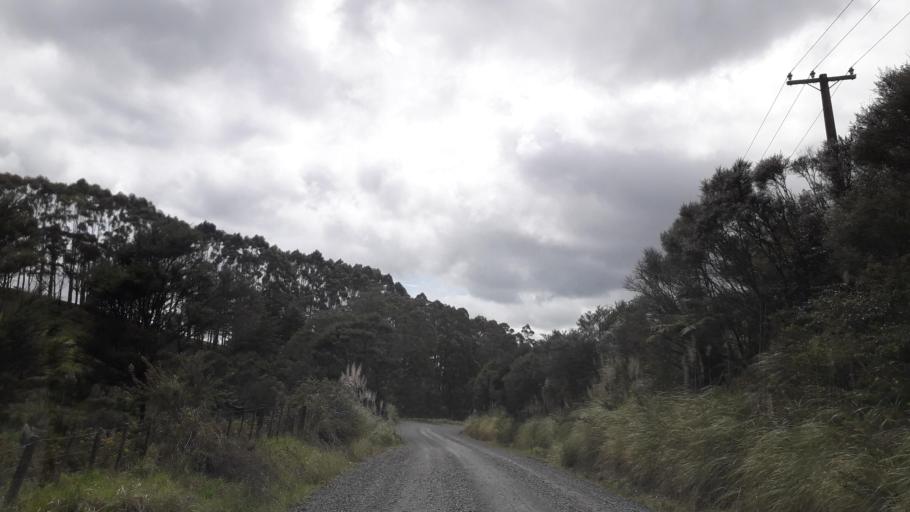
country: NZ
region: Northland
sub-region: Far North District
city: Kaitaia
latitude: -35.1573
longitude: 173.3438
